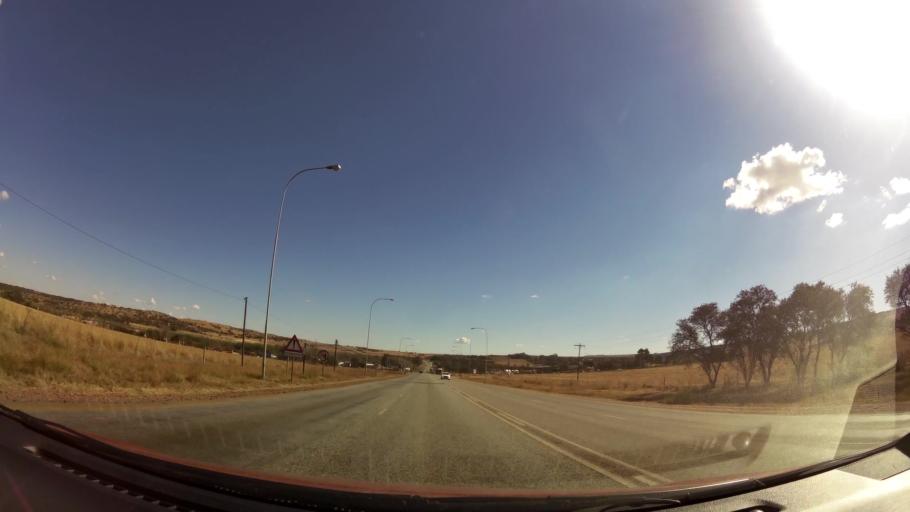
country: ZA
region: North-West
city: Fochville
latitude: -26.4413
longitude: 27.4864
